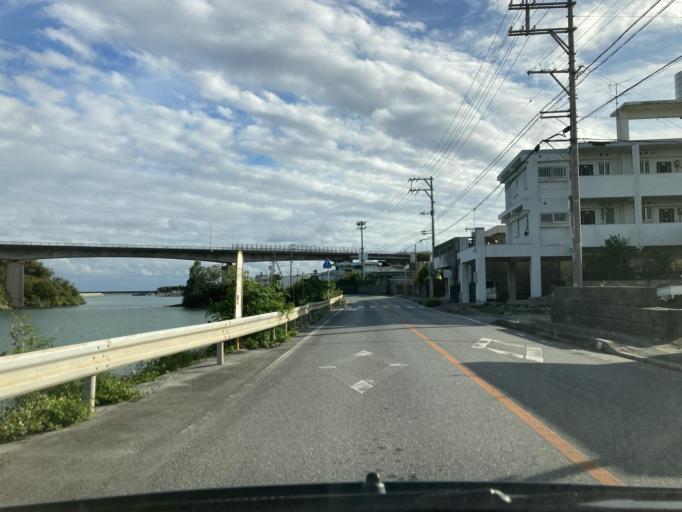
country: JP
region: Okinawa
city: Itoman
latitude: 26.1313
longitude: 127.7596
